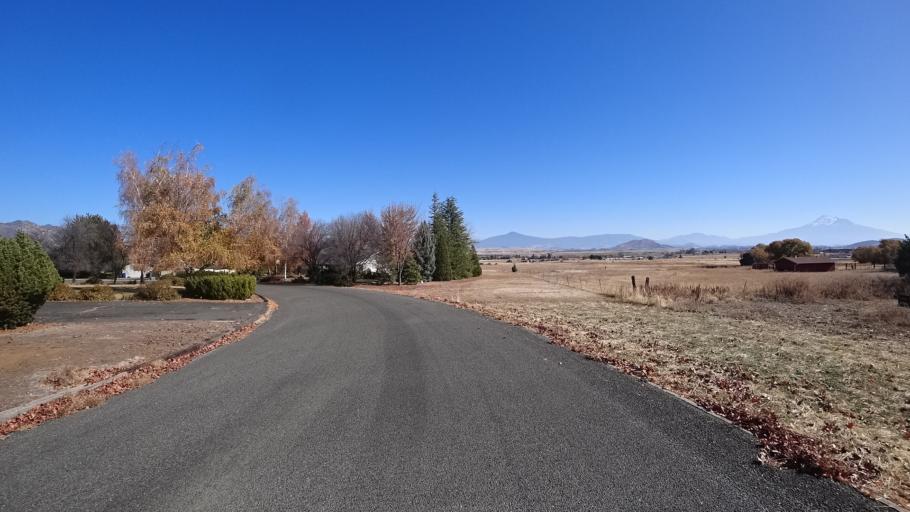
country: US
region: California
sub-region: Siskiyou County
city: Yreka
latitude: 41.7442
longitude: -122.6020
